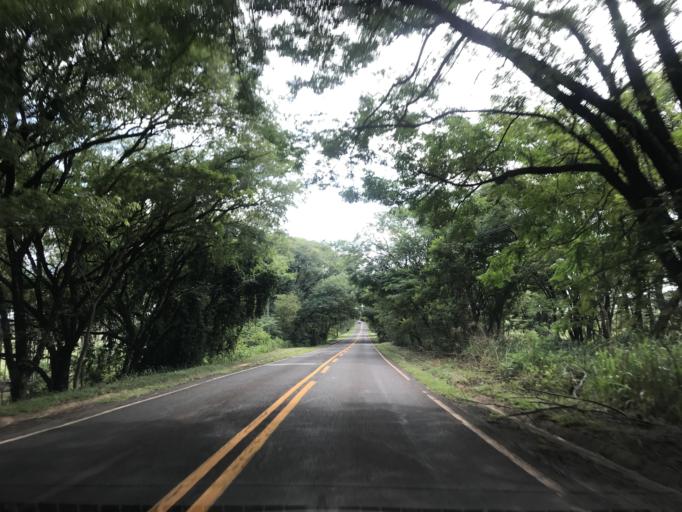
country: BR
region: Parana
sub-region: Terra Rica
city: Terra Rica
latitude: -22.7754
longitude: -52.6541
